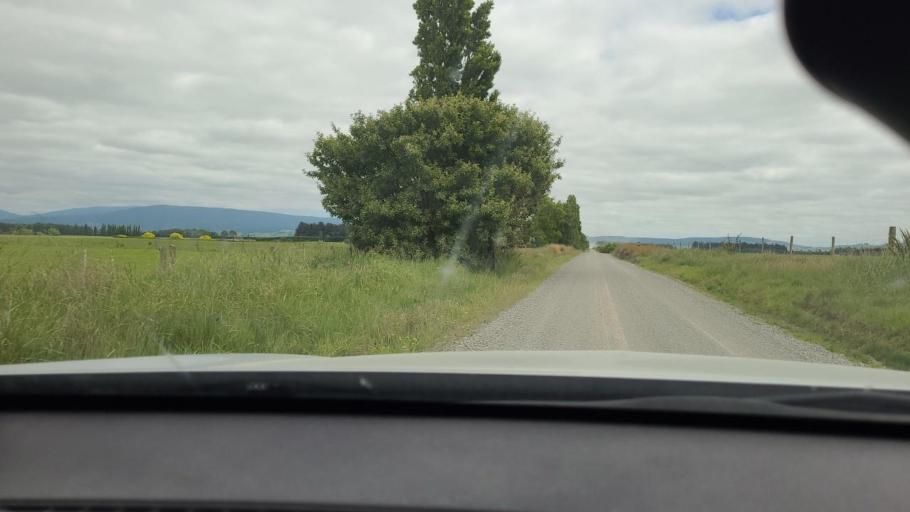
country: NZ
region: Southland
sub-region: Southland District
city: Riverton
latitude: -46.0658
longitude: 168.0408
